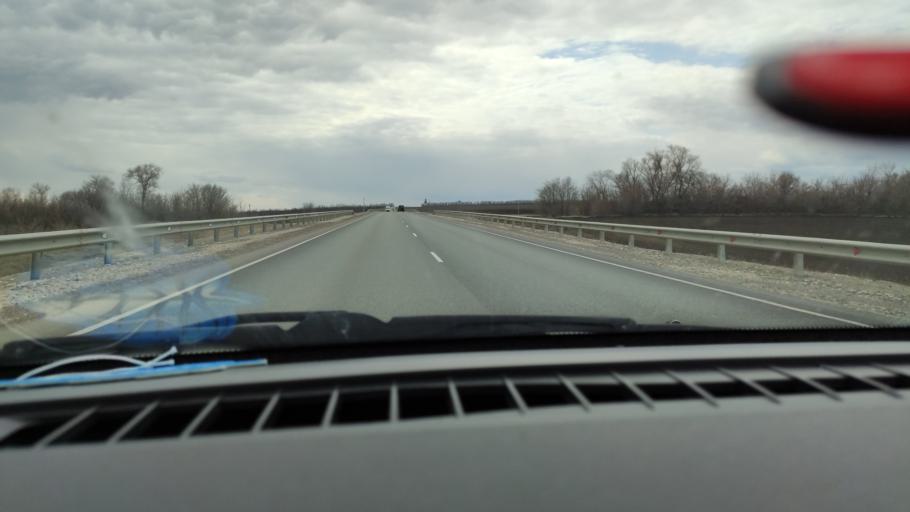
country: RU
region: Saratov
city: Yelshanka
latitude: 51.8429
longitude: 46.4801
